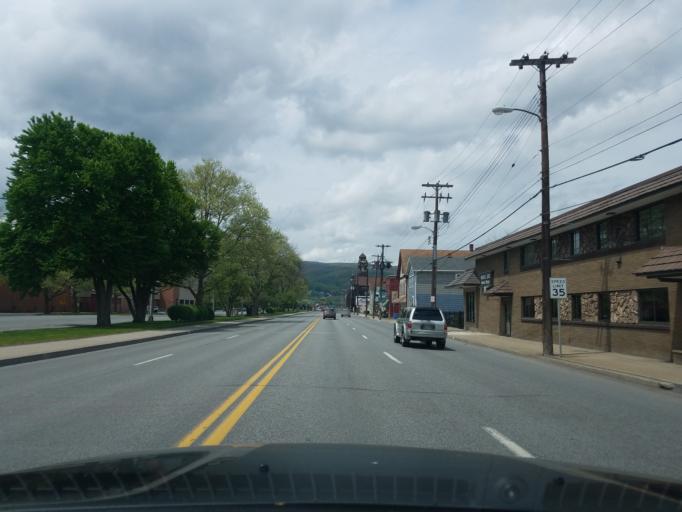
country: US
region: Pennsylvania
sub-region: Cambria County
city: Johnstown
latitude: 40.3410
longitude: -78.9314
